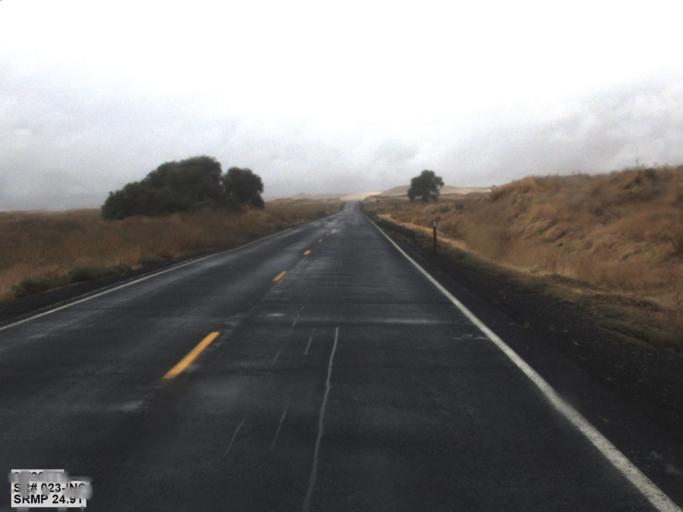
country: US
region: Washington
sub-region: Spokane County
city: Cheney
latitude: 47.1186
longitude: -117.7817
